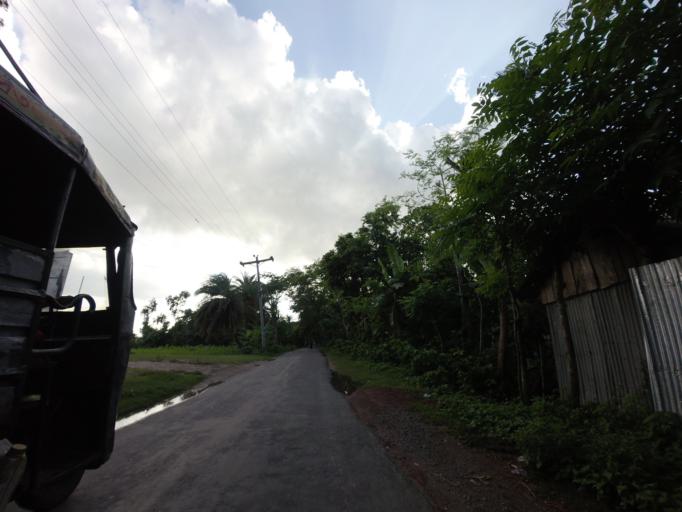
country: BD
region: Khulna
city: Kalia
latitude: 23.0369
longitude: 89.6259
